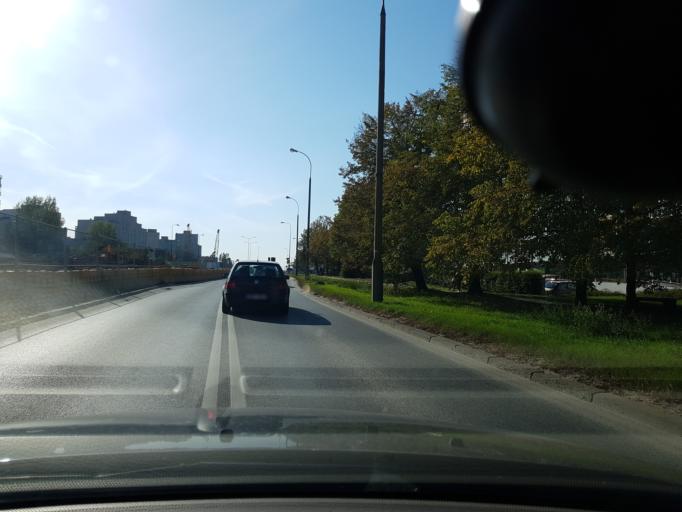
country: PL
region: Masovian Voivodeship
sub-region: Warszawa
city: Ursynow
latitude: 52.1431
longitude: 21.0468
